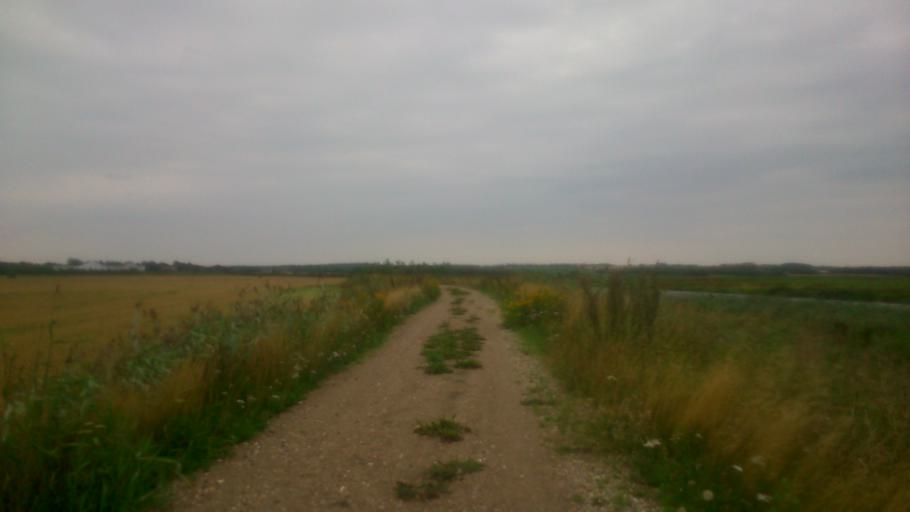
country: DK
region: Central Jutland
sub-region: Ringkobing-Skjern Kommune
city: Skjern
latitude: 55.9170
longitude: 8.4807
